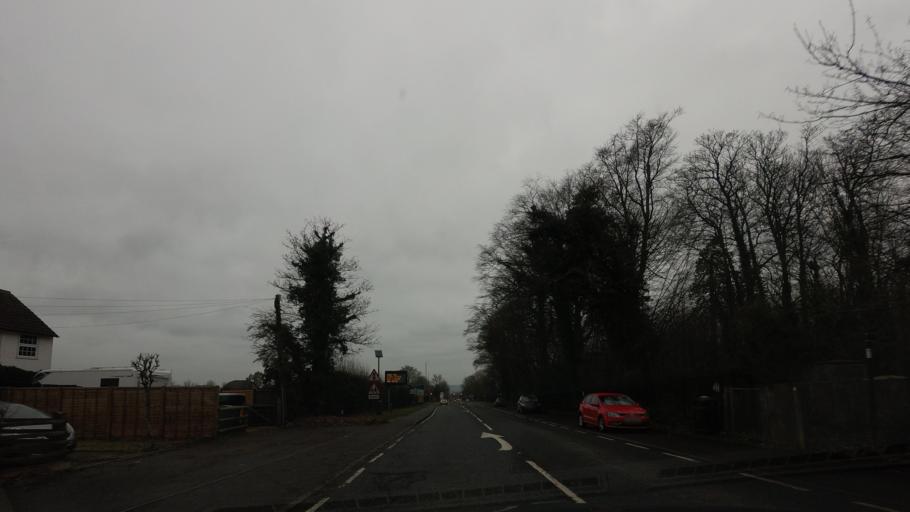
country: GB
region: England
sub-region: Kent
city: Maidstone
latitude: 51.2287
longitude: 0.5122
